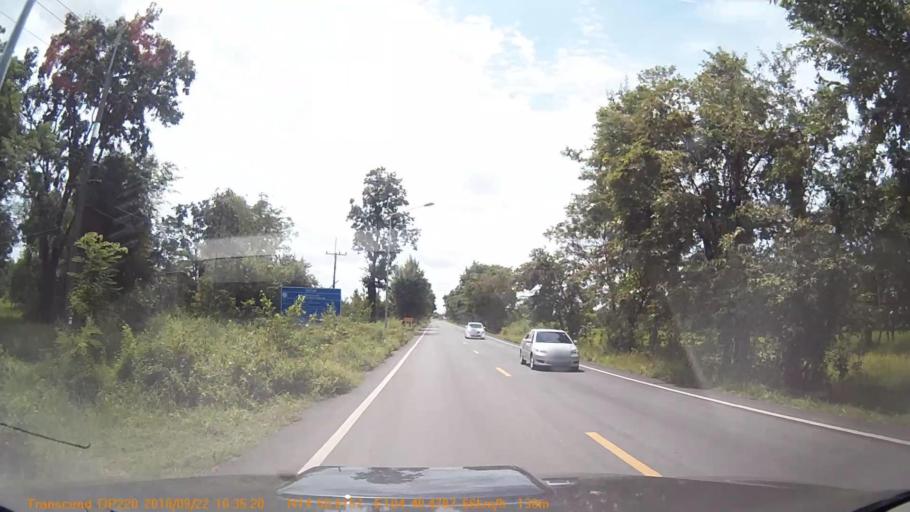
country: TH
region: Sisaket
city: Benchalak
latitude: 14.8437
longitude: 104.6746
